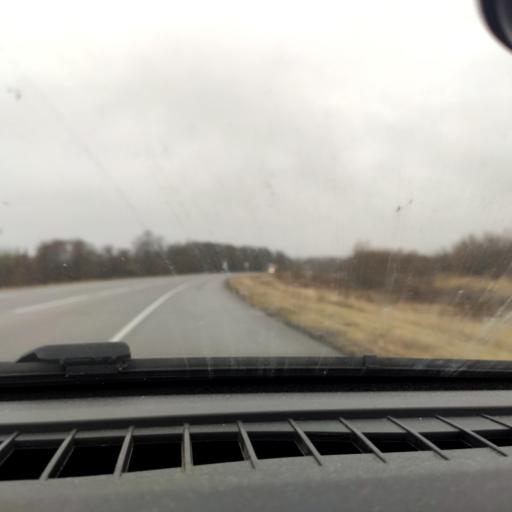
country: RU
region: Voronezj
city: Kolodeznyy
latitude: 51.3145
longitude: 39.0291
